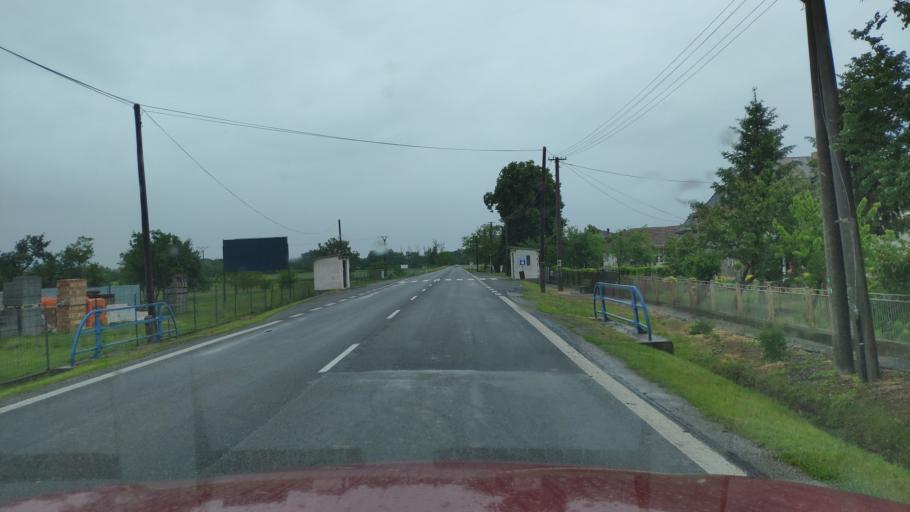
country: HU
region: Borsod-Abauj-Zemplen
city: Karcsa
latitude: 48.4284
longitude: 21.8468
